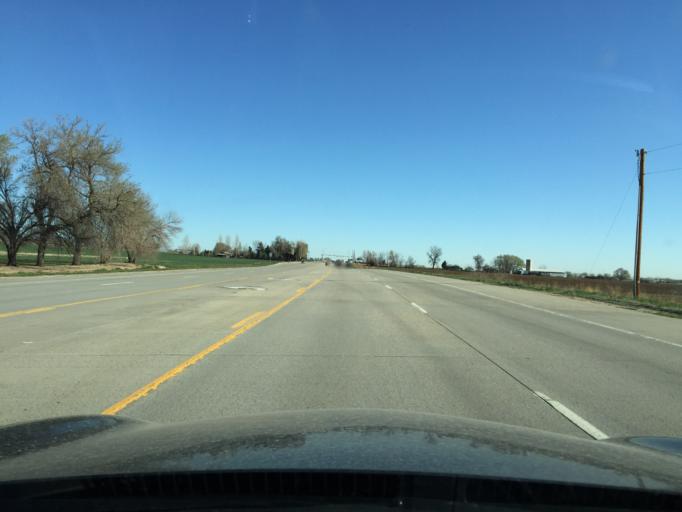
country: US
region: Colorado
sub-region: Boulder County
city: Erie
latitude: 40.0820
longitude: -105.1026
